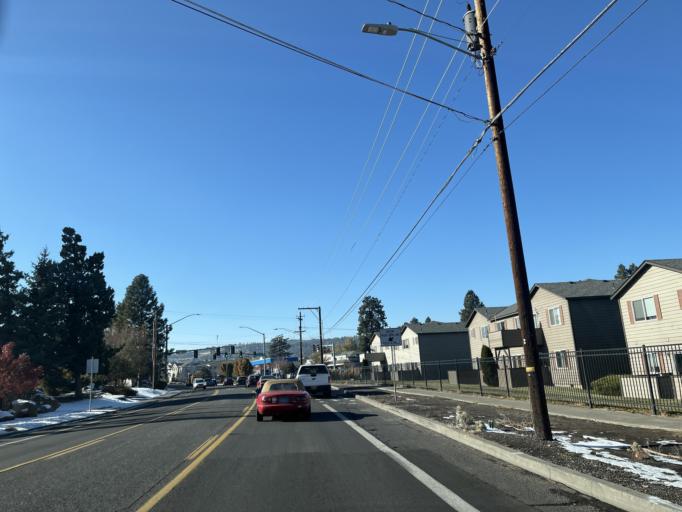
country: US
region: Oregon
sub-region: Deschutes County
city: Bend
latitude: 44.0765
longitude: -121.2940
